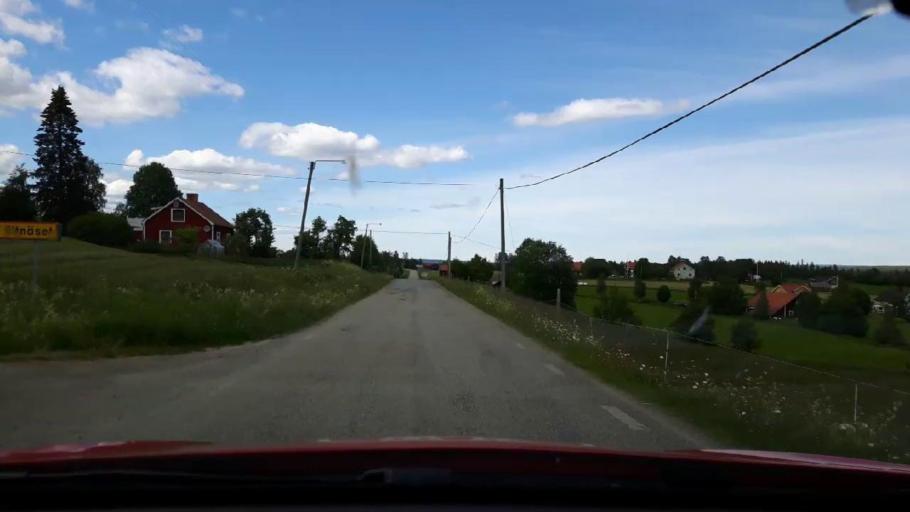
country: SE
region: Jaemtland
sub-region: Bergs Kommun
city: Hoverberg
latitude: 62.8266
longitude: 14.4598
